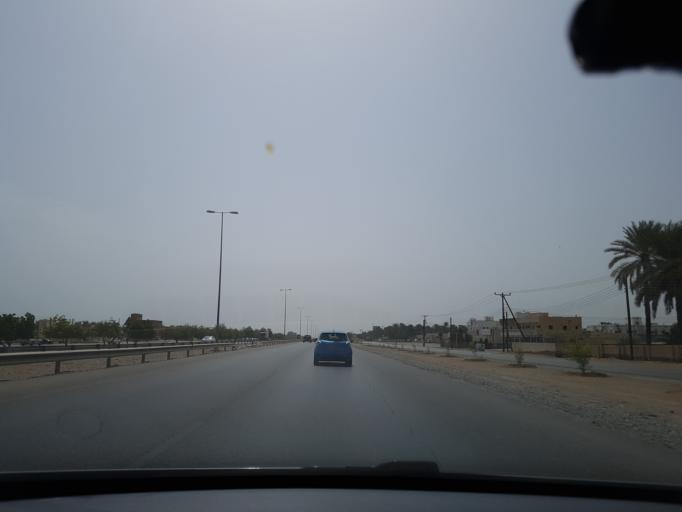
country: OM
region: Al Batinah
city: As Suwayq
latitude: 23.8366
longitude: 57.3853
